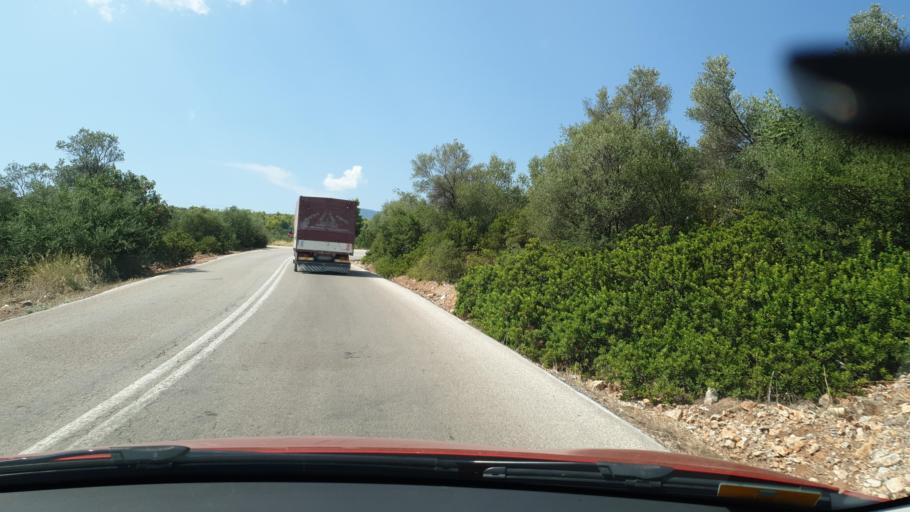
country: GR
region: Central Greece
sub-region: Nomos Evvoias
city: Psachna
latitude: 38.5880
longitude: 23.6084
